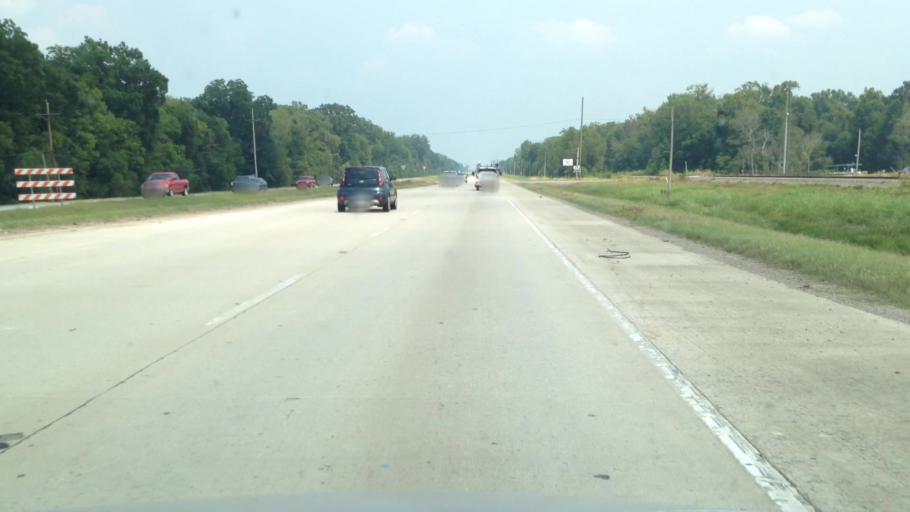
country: US
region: Louisiana
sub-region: West Baton Rouge Parish
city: Erwinville
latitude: 30.5077
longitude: -91.3324
